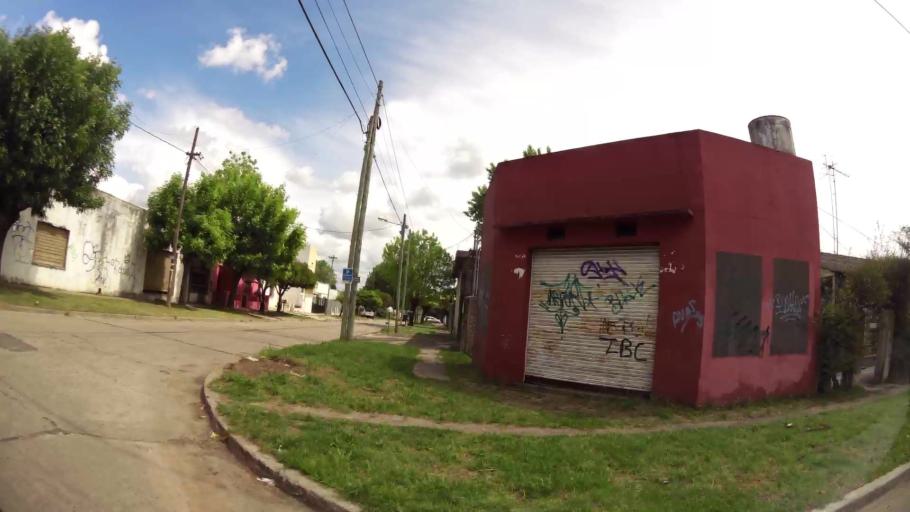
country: AR
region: Buenos Aires
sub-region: Partido de Quilmes
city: Quilmes
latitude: -34.7827
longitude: -58.2707
